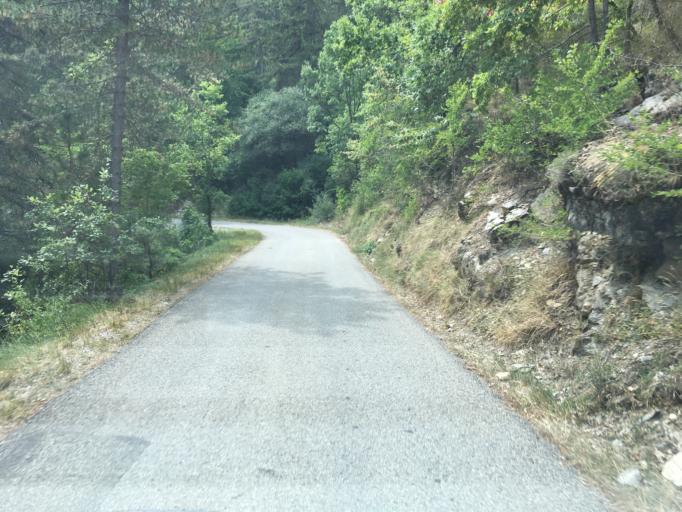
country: FR
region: Provence-Alpes-Cote d'Azur
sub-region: Departement des Alpes-de-Haute-Provence
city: Digne-les-Bains
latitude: 44.2106
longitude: 6.1498
